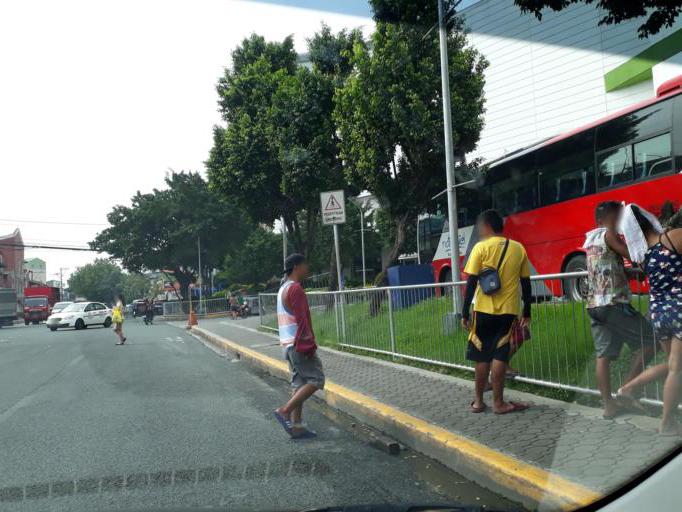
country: PH
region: Metro Manila
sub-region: City of Manila
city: Manila
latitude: 14.6178
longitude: 120.9851
